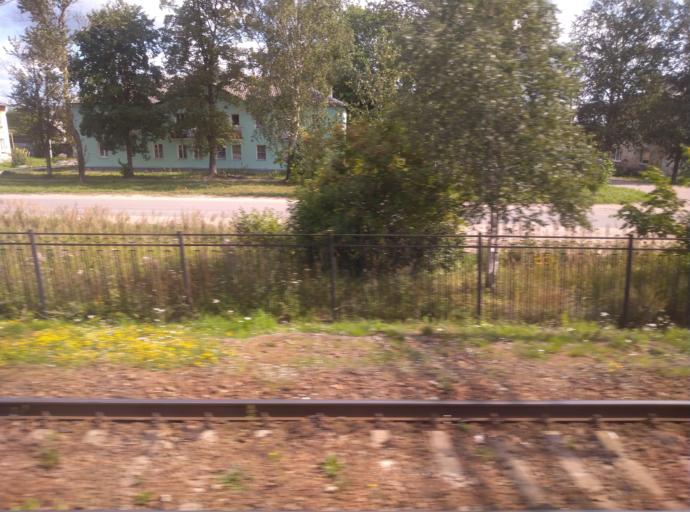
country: RU
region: Leningrad
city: Ul'yanovka
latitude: 59.6346
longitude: 30.7590
